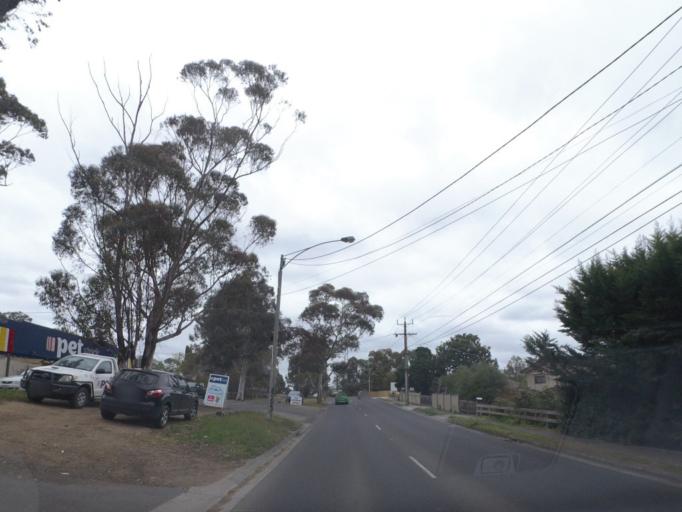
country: AU
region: Victoria
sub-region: Nillumbik
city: Eltham North
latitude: -37.7066
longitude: 145.1509
